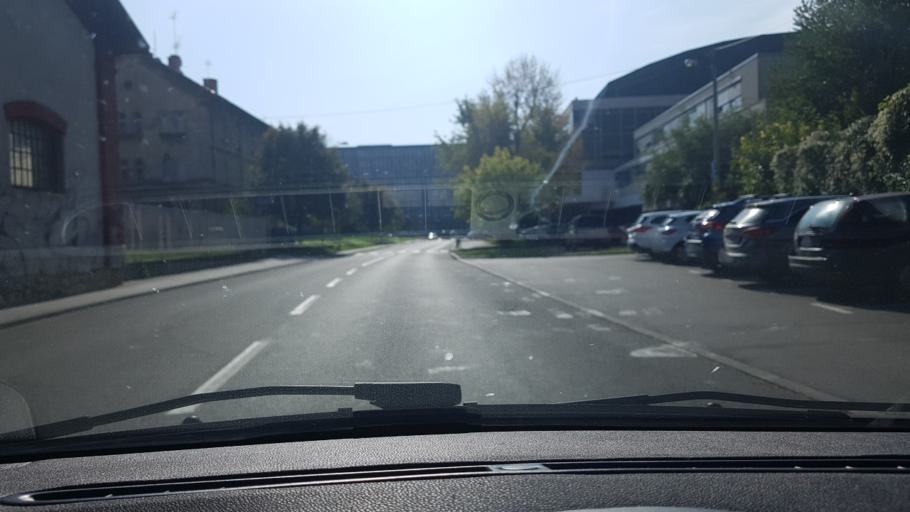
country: HR
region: Grad Zagreb
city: Zagreb - Centar
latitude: 45.8022
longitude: 15.9808
